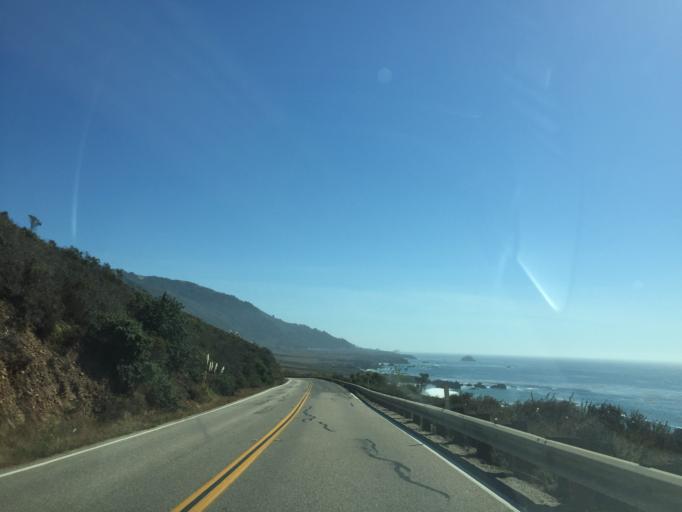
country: US
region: California
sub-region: Monterey County
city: Greenfield
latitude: 35.9531
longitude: -121.4810
